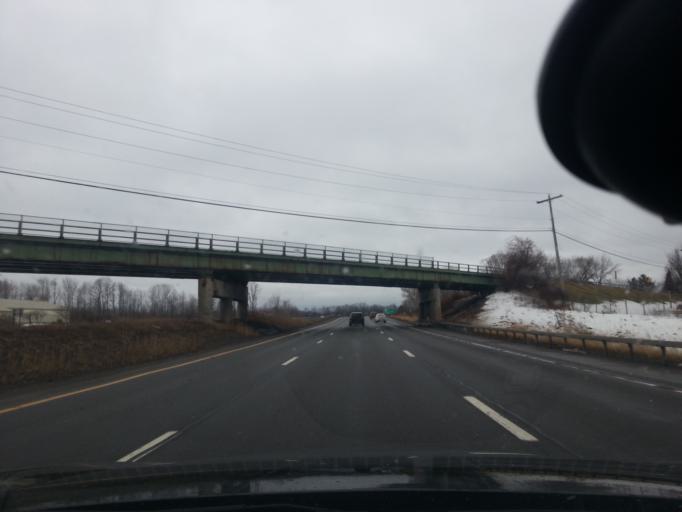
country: US
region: New York
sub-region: Onondaga County
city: North Syracuse
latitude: 43.1503
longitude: -76.1103
